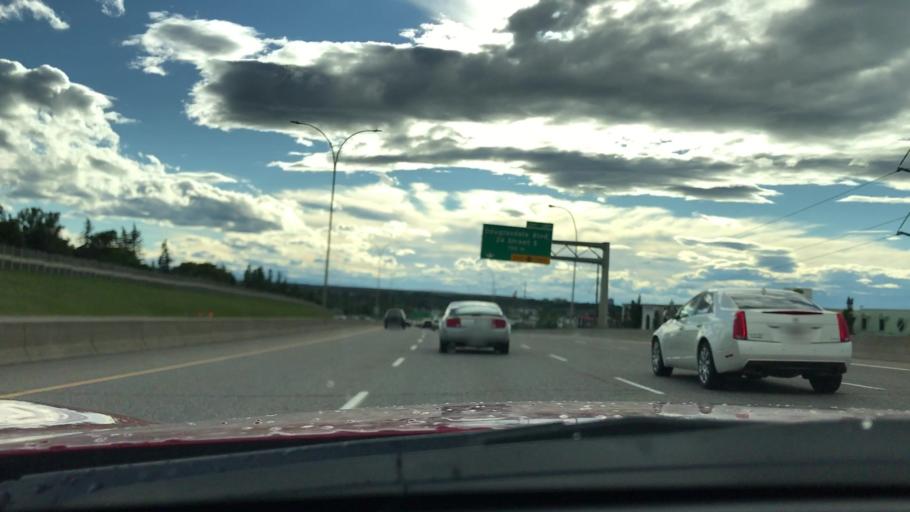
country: CA
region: Alberta
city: Calgary
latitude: 50.9469
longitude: -113.9886
